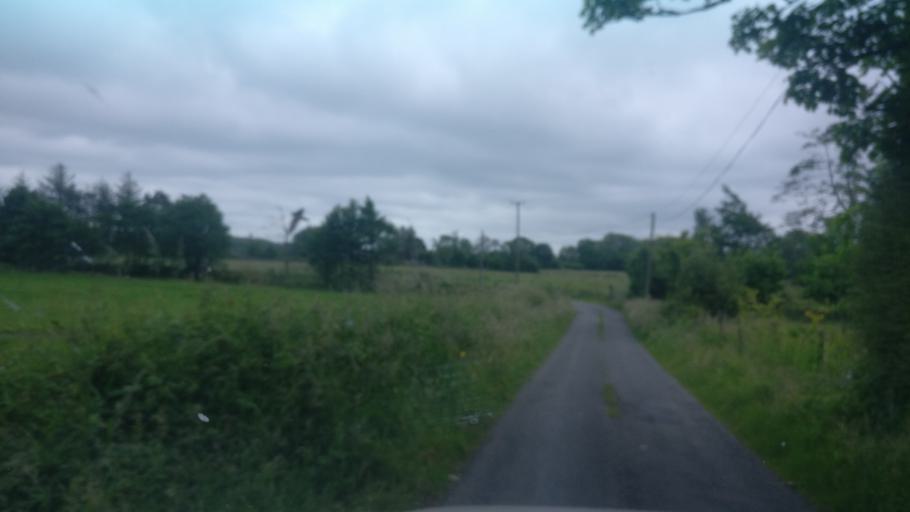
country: IE
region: Connaught
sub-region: County Galway
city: Ballinasloe
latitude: 53.3038
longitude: -8.3510
